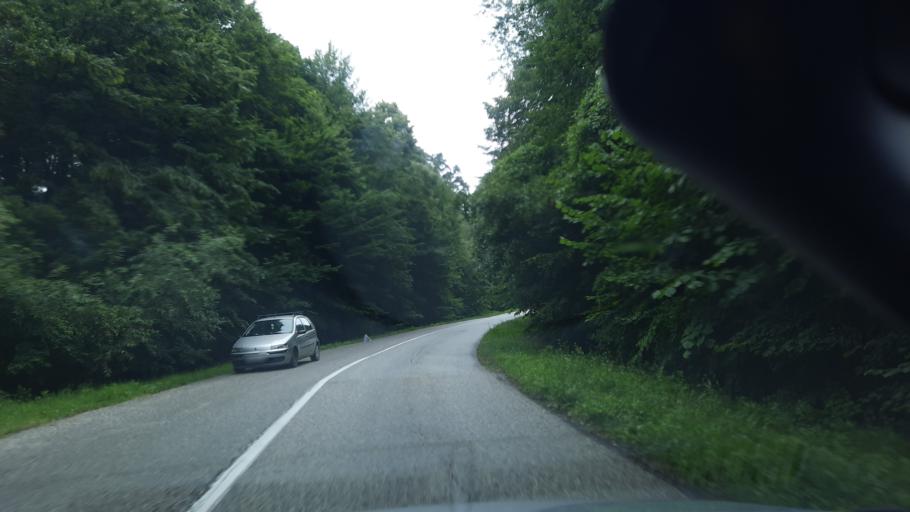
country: RS
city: Glozan
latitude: 45.1425
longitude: 19.5799
